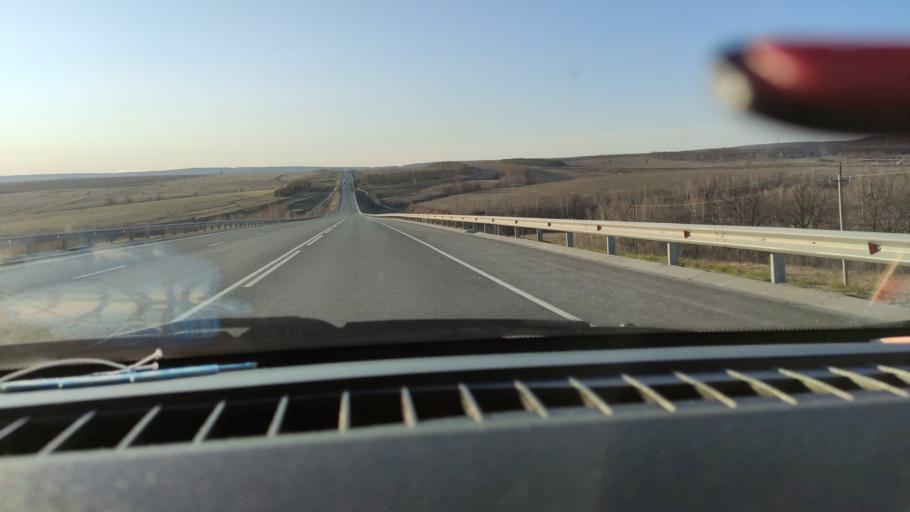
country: RU
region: Saratov
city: Shikhany
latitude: 52.1408
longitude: 47.2084
